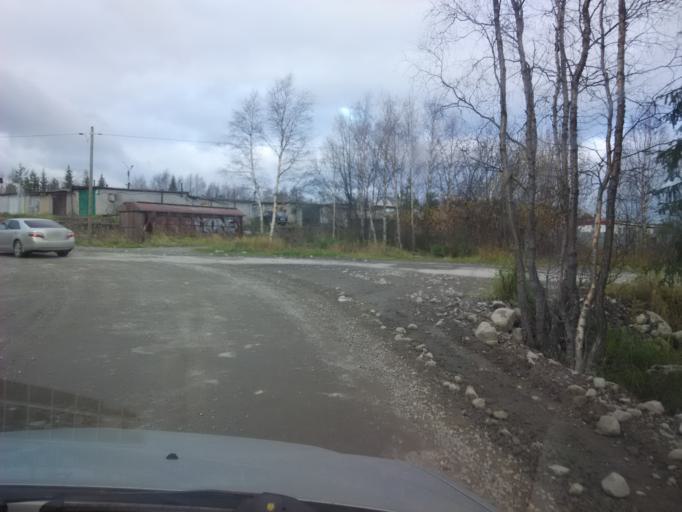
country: RU
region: Murmansk
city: Polyarnyye Zori
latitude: 67.3802
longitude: 32.5108
